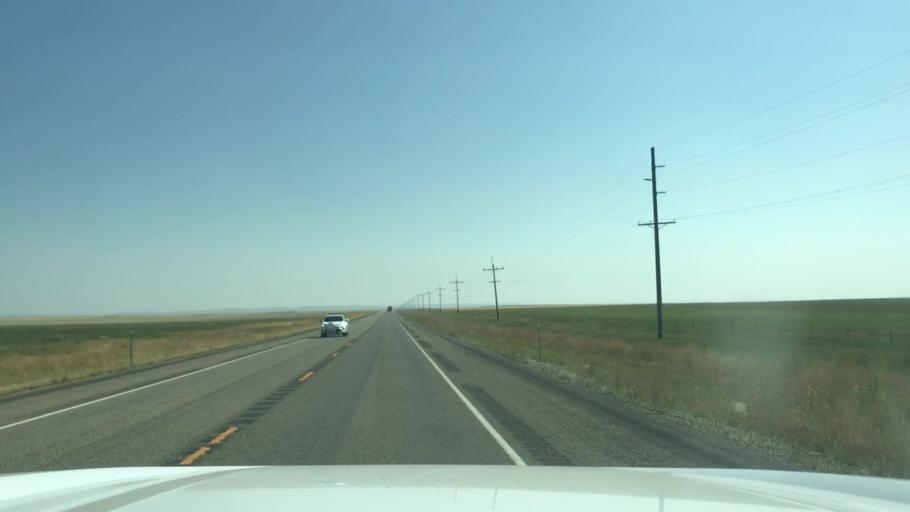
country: US
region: Montana
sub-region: Wheatland County
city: Harlowton
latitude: 46.5158
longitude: -109.7660
